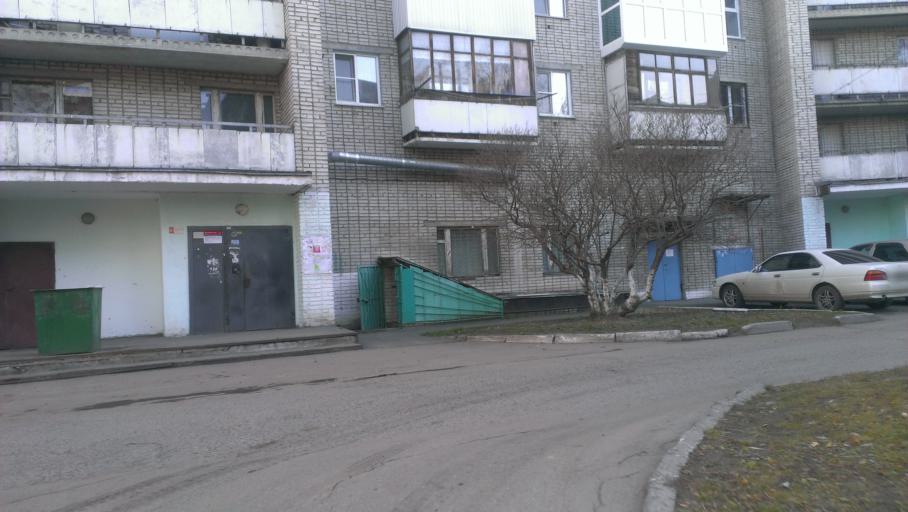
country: RU
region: Altai Krai
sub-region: Gorod Barnaulskiy
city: Barnaul
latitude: 53.3440
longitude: 83.6943
